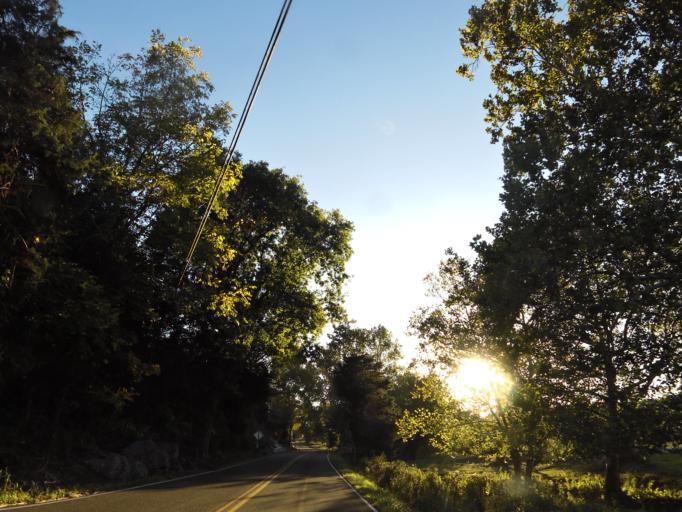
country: US
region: Tennessee
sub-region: Grainger County
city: Rutledge
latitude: 36.3131
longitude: -83.5467
